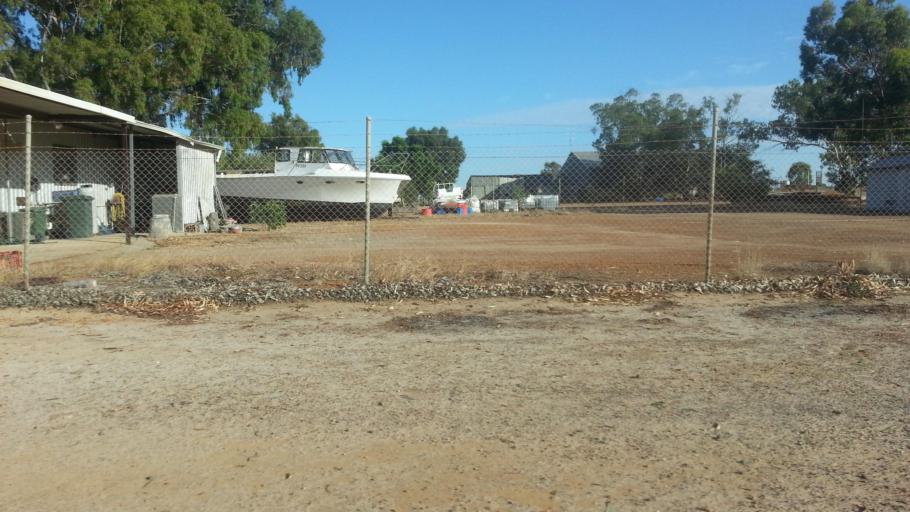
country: AU
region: Western Australia
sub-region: Dandaragan
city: Jurien Bay
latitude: -29.8182
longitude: 115.2739
